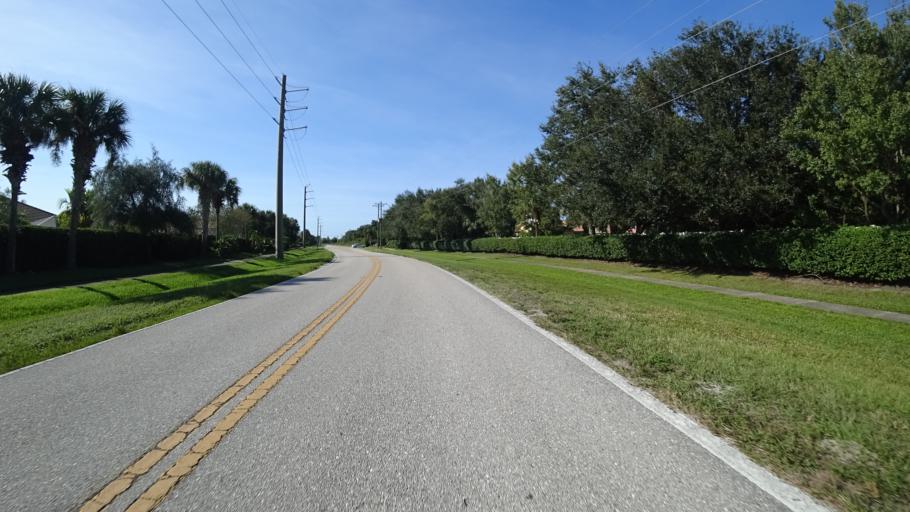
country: US
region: Florida
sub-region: Sarasota County
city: Desoto Lakes
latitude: 27.4195
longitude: -82.4640
